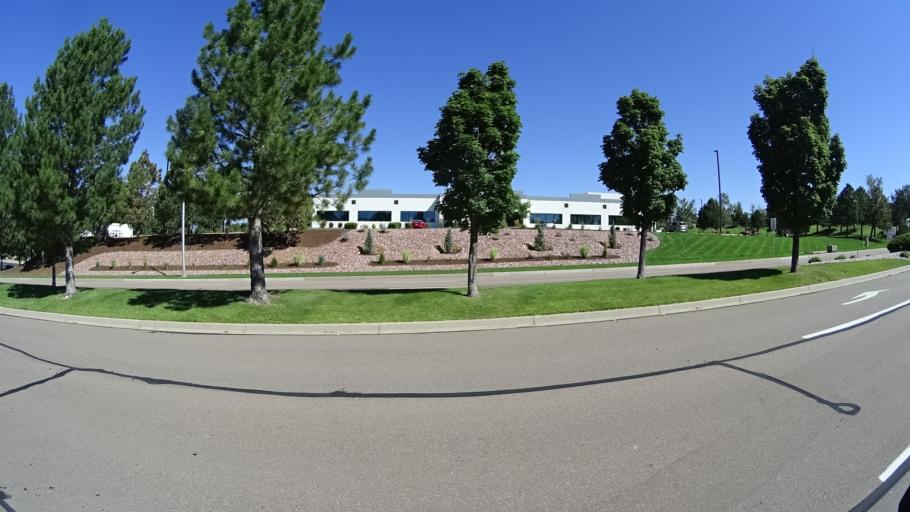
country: US
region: Colorado
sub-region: El Paso County
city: Air Force Academy
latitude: 38.9571
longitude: -104.7882
